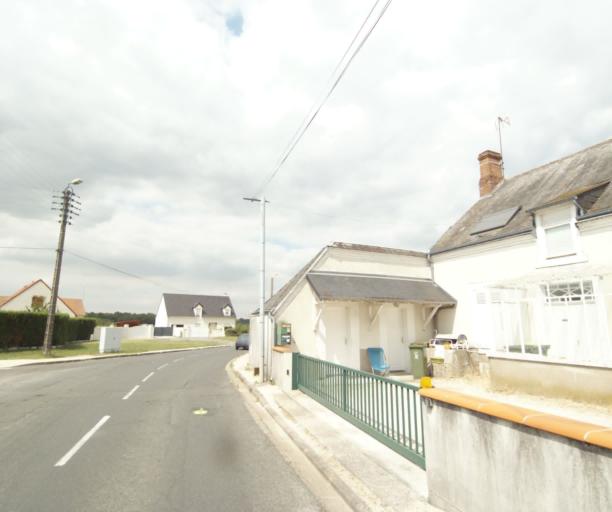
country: FR
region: Centre
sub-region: Departement du Loiret
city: Saran
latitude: 47.9327
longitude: 1.8655
